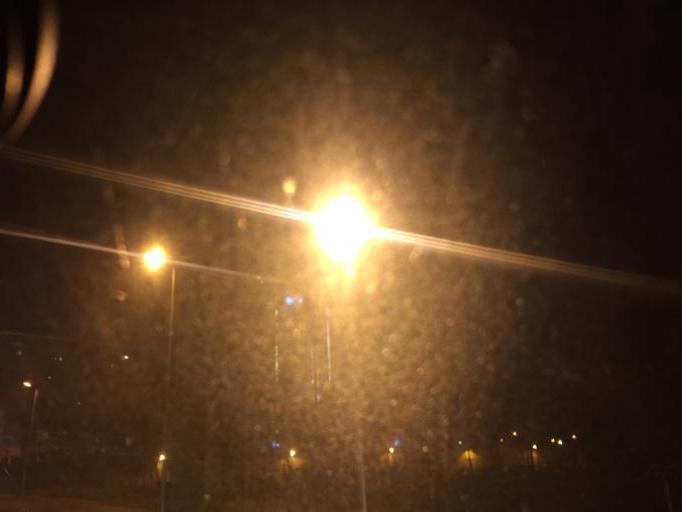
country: EG
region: Alexandria
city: Alexandria
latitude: 31.2824
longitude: 30.0130
